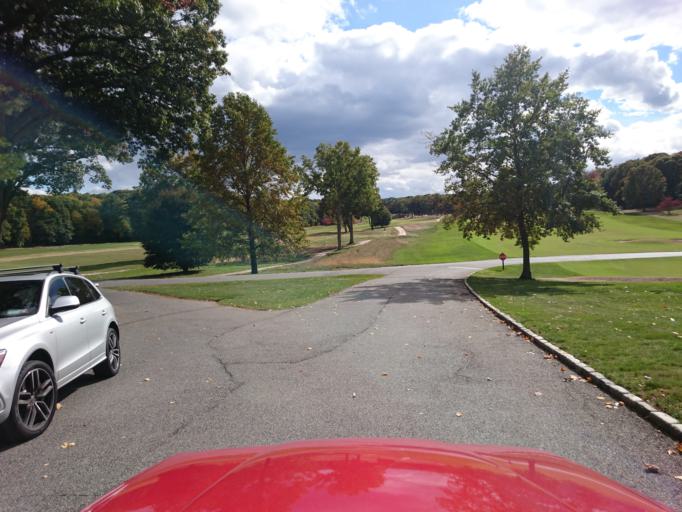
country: US
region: New York
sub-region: Nassau County
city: Locust Valley
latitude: 40.8558
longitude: -73.5843
